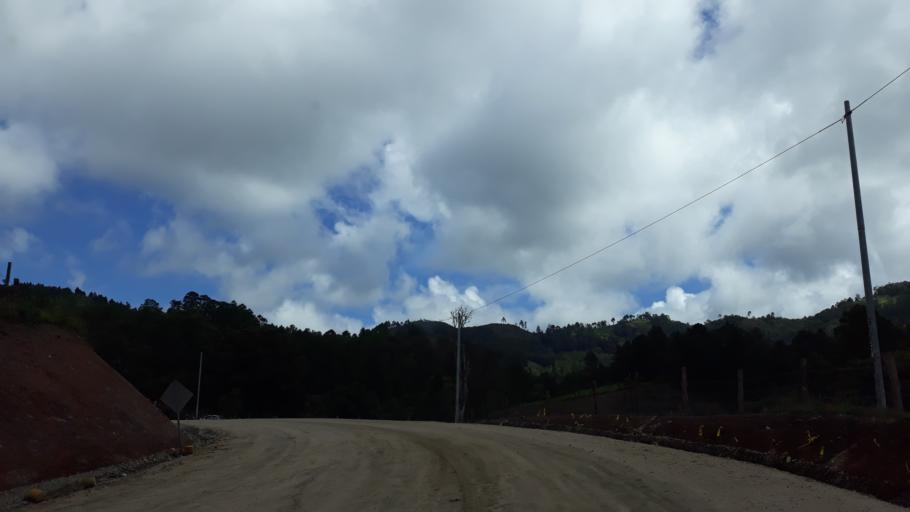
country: HN
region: El Paraiso
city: Santa Cruz
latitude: 13.7654
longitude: -86.6327
